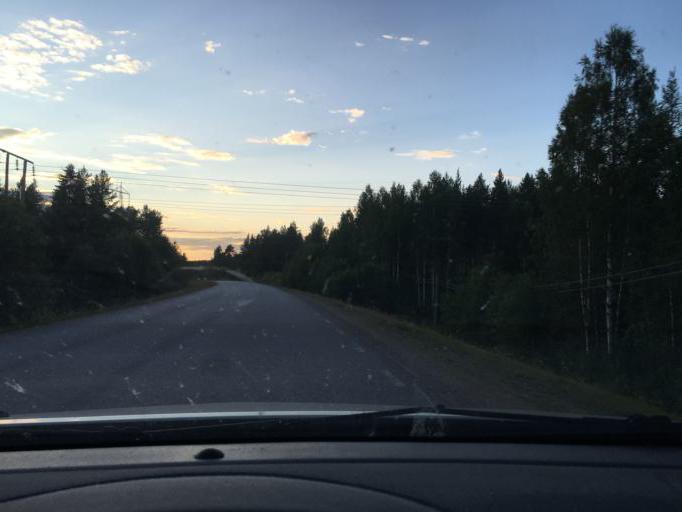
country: SE
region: Norrbotten
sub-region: Kalix Kommun
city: Rolfs
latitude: 65.9076
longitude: 22.9301
